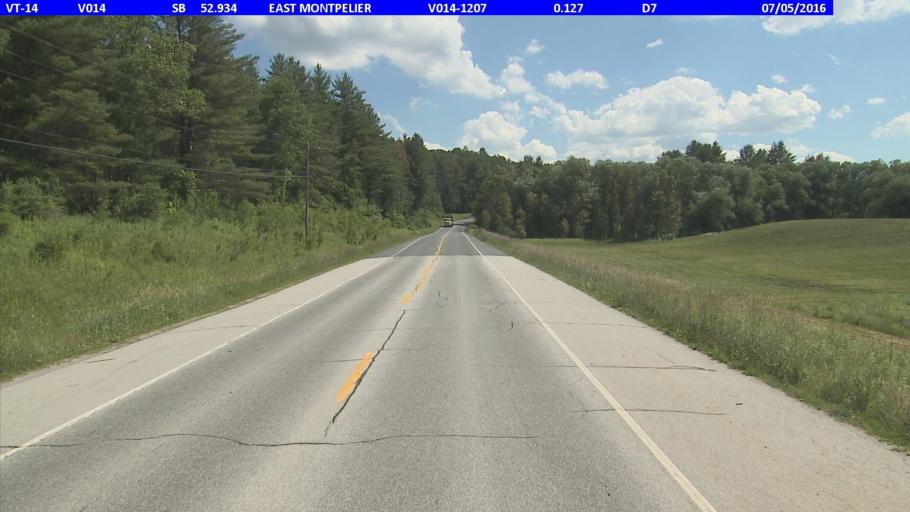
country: US
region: Vermont
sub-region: Washington County
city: Barre
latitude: 44.2372
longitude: -72.4887
